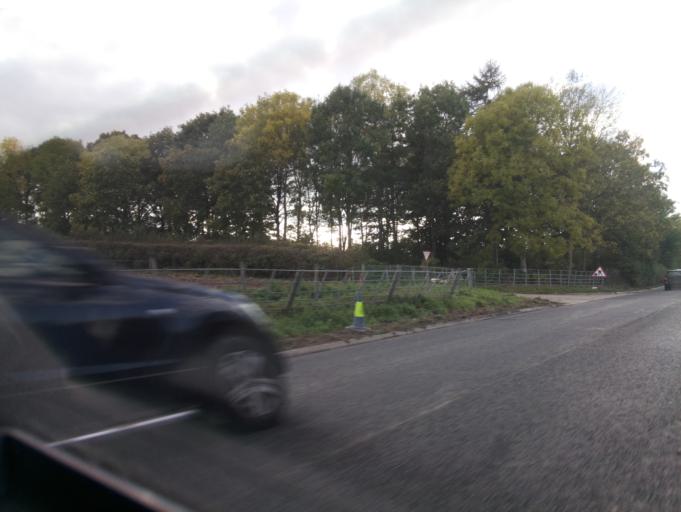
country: GB
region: England
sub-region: Herefordshire
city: Ocle Pychard
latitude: 52.0649
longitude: -2.5662
